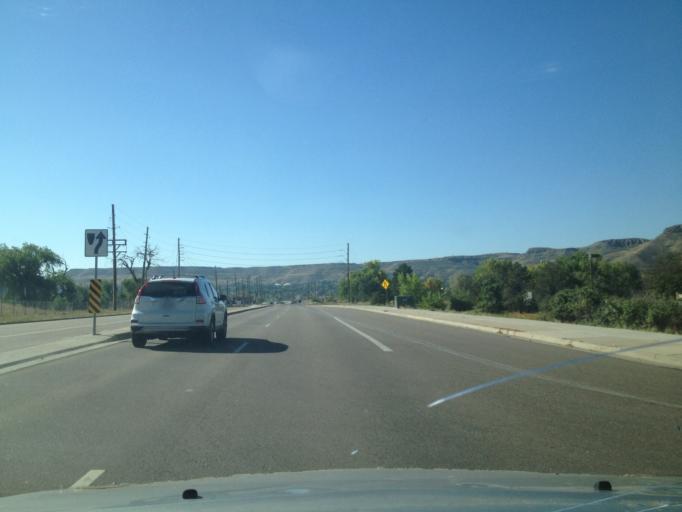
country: US
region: Colorado
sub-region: Jefferson County
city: Applewood
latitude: 39.7795
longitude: -105.1749
